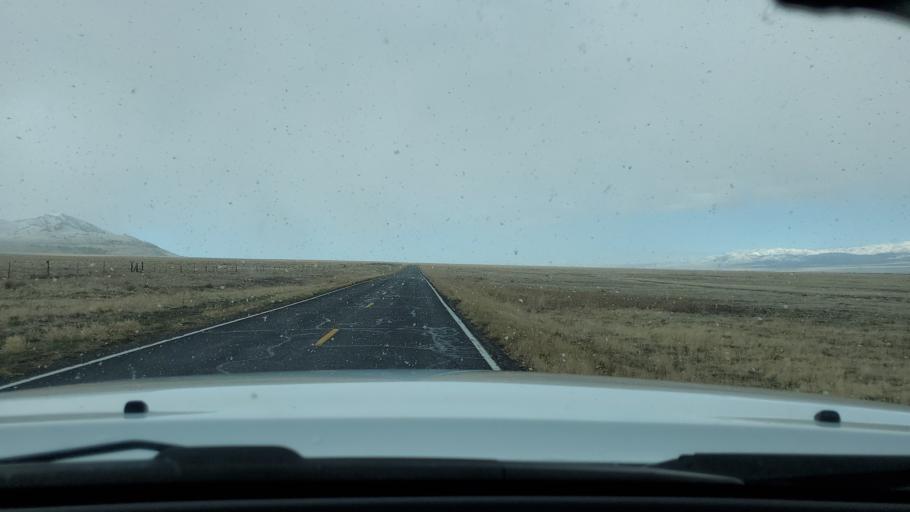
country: US
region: Utah
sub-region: Tooele County
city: Grantsville
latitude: 40.6055
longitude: -112.7086
